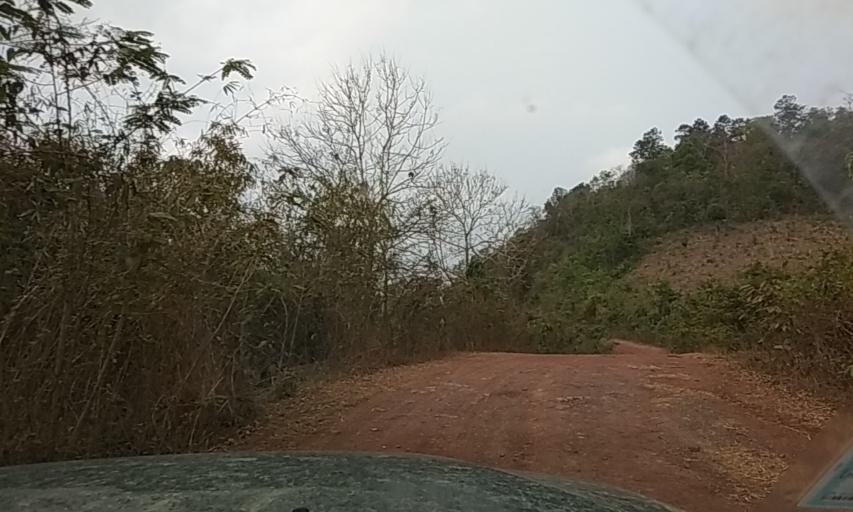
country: TH
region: Nan
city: Mae Charim
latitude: 18.4210
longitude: 101.1720
